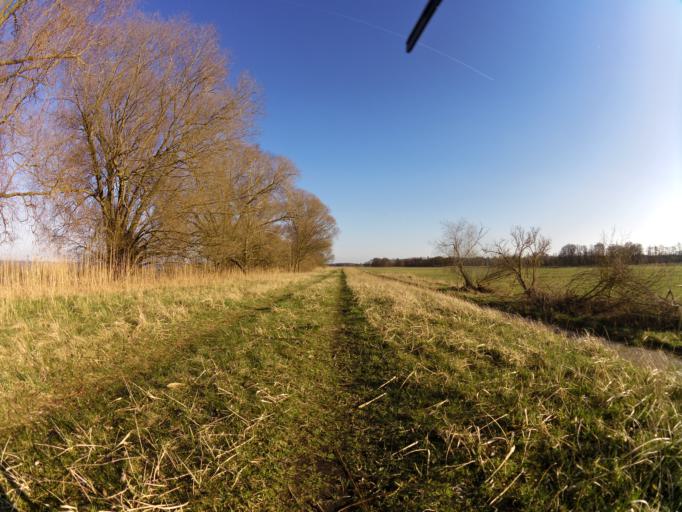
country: PL
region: West Pomeranian Voivodeship
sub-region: Powiat policki
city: Nowe Warpno
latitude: 53.7149
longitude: 14.3440
